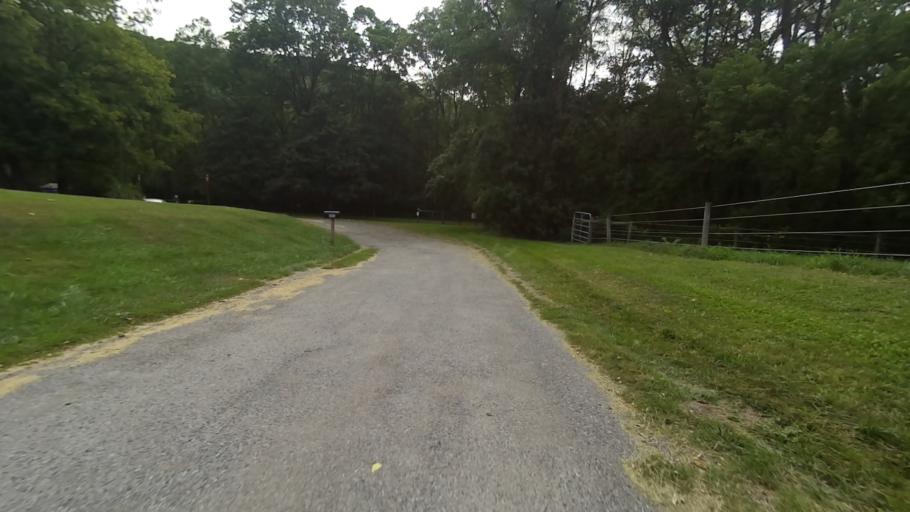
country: US
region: Pennsylvania
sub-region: Blair County
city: Williamsburg
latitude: 40.4872
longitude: -78.1705
